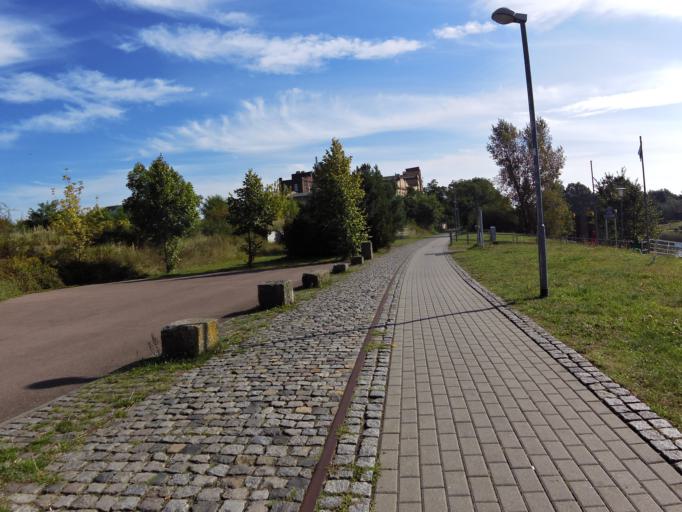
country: DE
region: Saxony-Anhalt
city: Wittenburg
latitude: 51.8643
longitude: 12.6225
